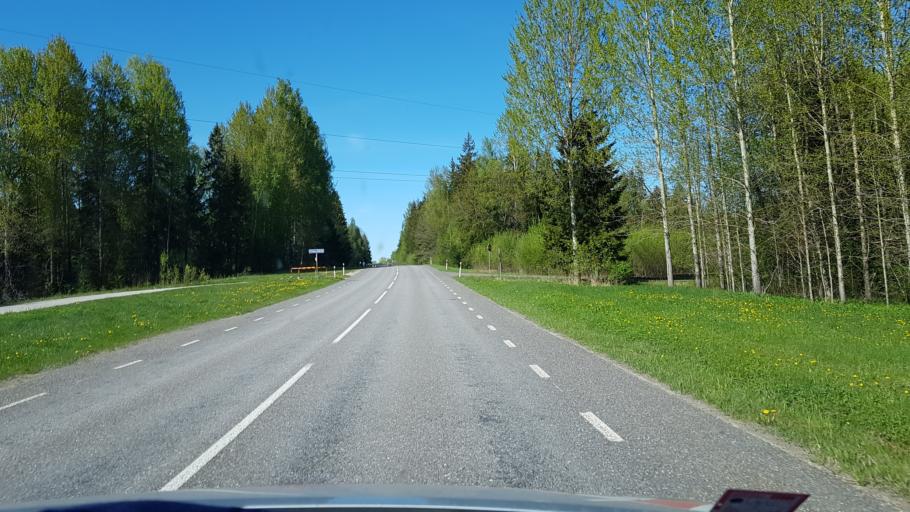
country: EE
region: Tartu
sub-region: Elva linn
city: Elva
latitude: 58.0384
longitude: 26.4405
